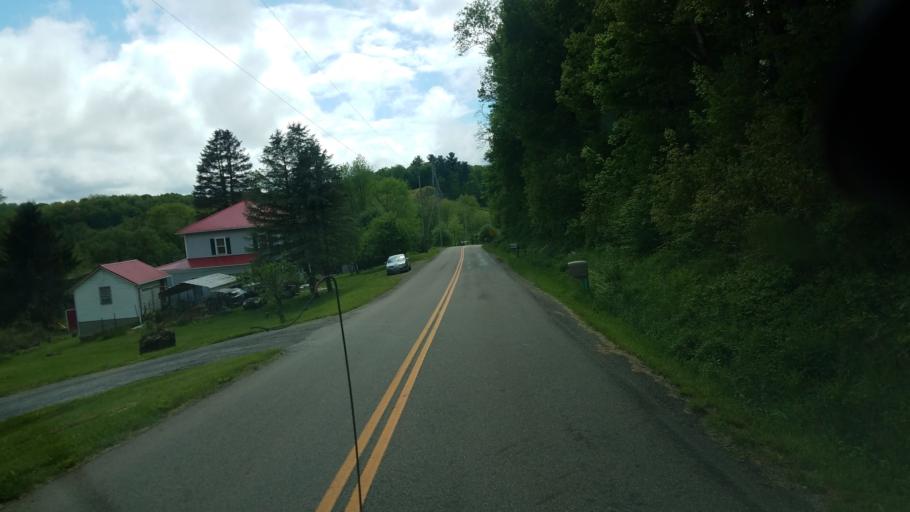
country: US
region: Ohio
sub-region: Tuscarawas County
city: Strasburg
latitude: 40.6423
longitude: -81.5053
